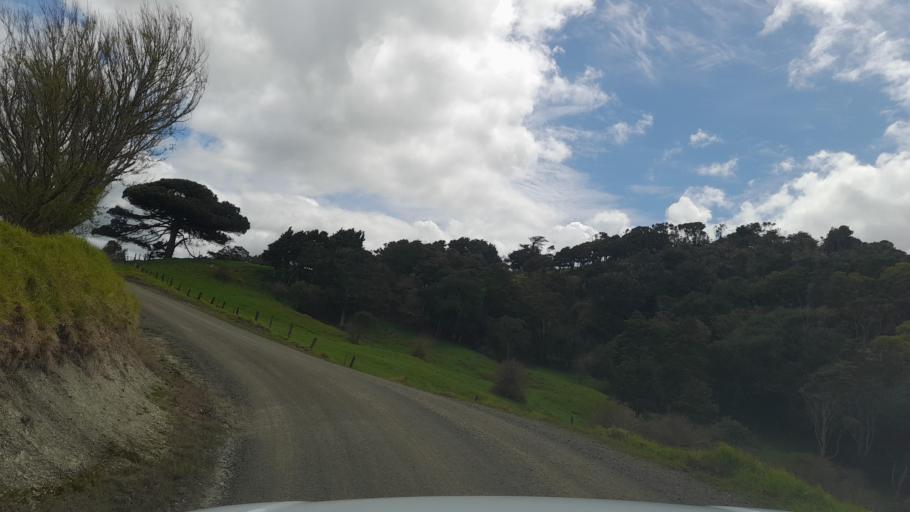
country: NZ
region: Auckland
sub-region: Auckland
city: Wellsford
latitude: -36.2175
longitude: 174.3210
